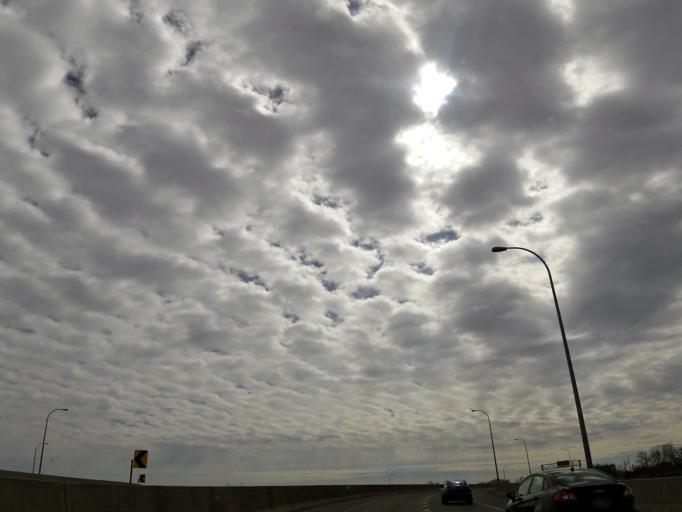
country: US
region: Minnesota
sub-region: Hennepin County
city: Richfield
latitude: 44.8926
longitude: -93.2756
